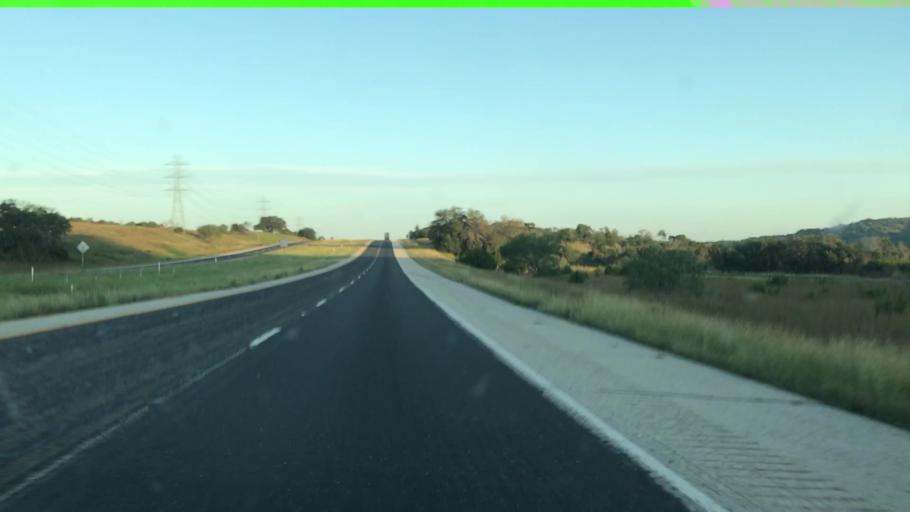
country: US
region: Texas
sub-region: Kerr County
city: Kerrville
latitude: 30.0518
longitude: -99.0098
